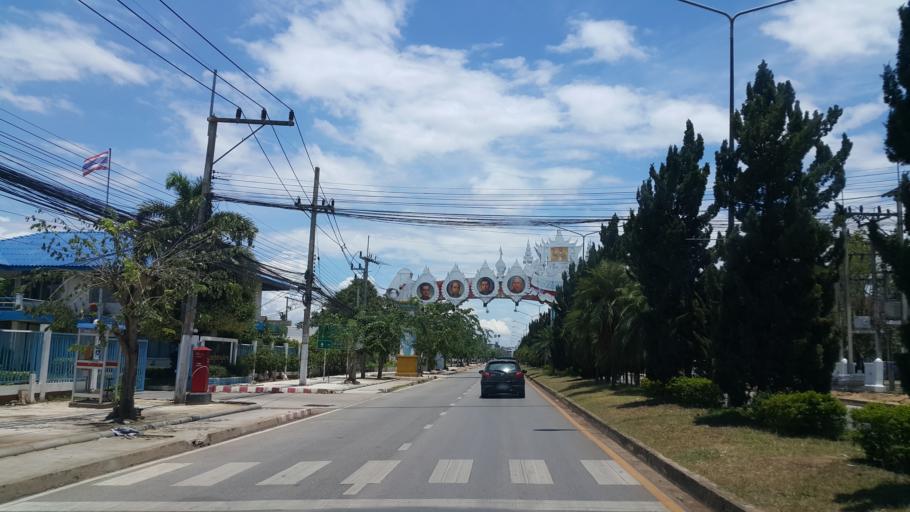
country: TH
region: Phayao
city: Phayao
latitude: 19.1761
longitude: 99.8910
